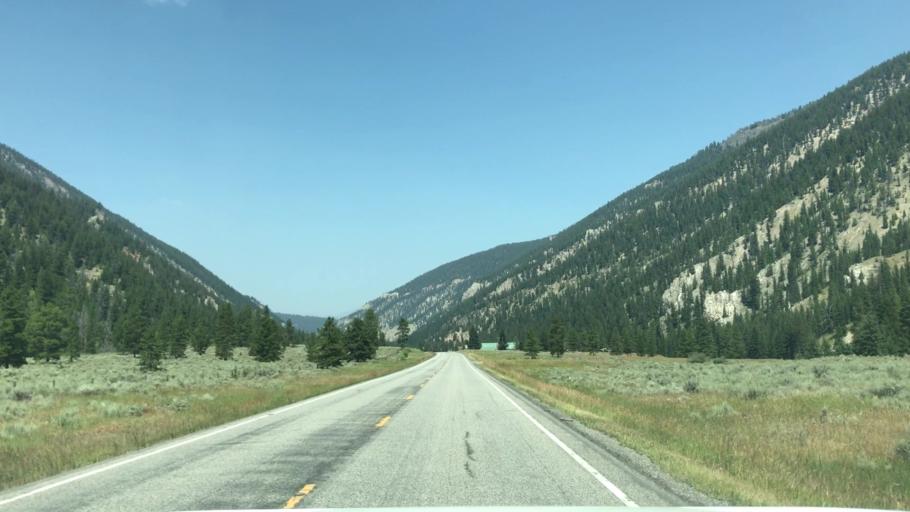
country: US
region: Montana
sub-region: Gallatin County
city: Big Sky
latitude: 45.1109
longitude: -111.2238
